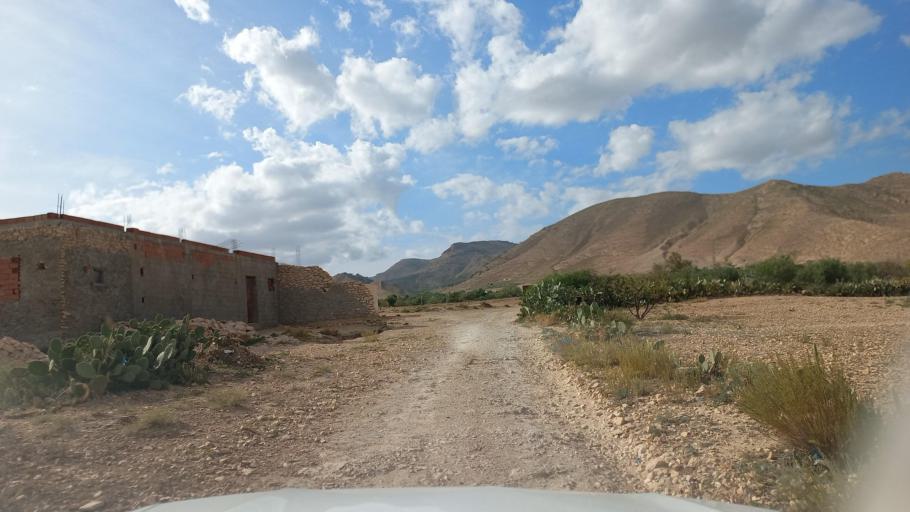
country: TN
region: Al Qasrayn
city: Sbiba
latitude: 35.4507
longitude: 9.0733
